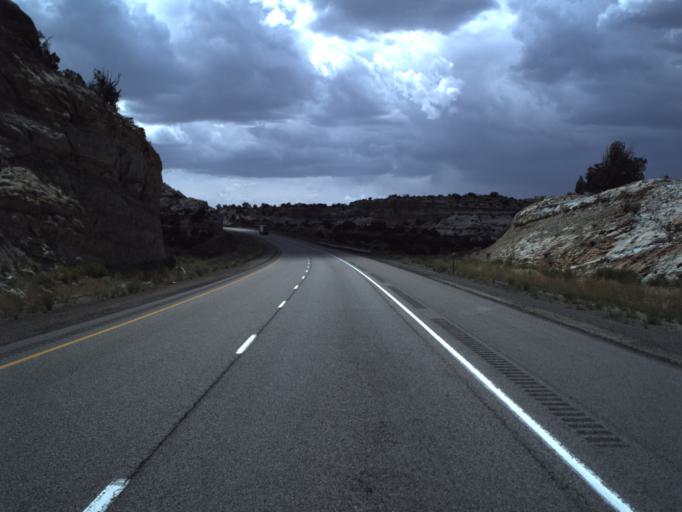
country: US
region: Utah
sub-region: Emery County
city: Ferron
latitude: 38.8546
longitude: -110.8769
